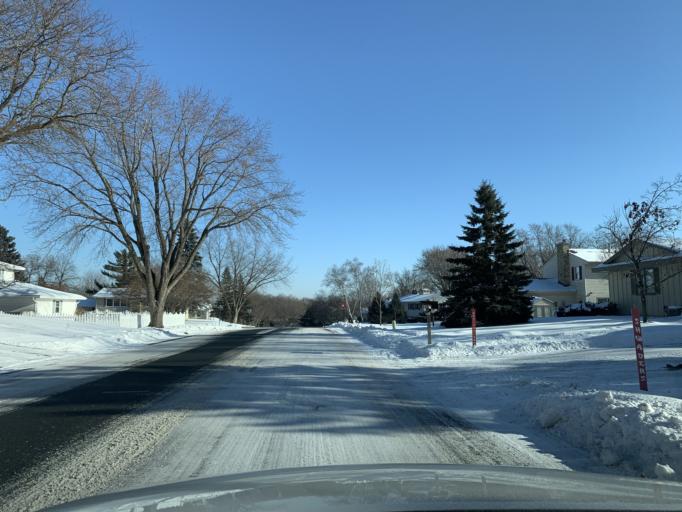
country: US
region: Minnesota
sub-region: Hennepin County
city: Bloomington
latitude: 44.8241
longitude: -93.3391
